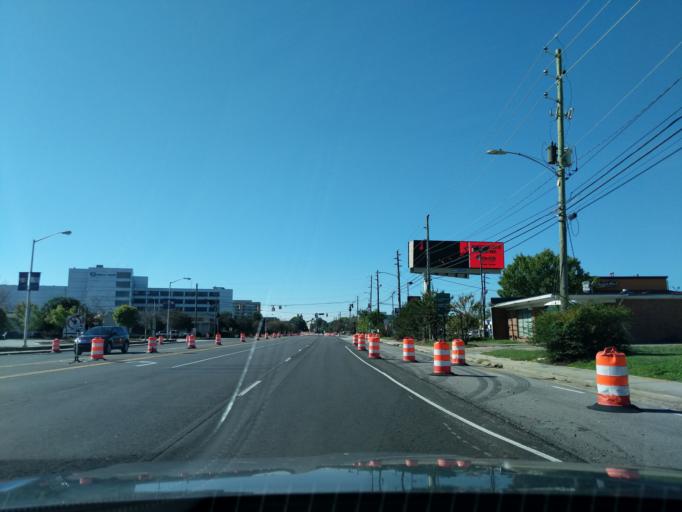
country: US
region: Georgia
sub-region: Richmond County
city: Augusta
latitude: 33.4762
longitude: -81.9866
